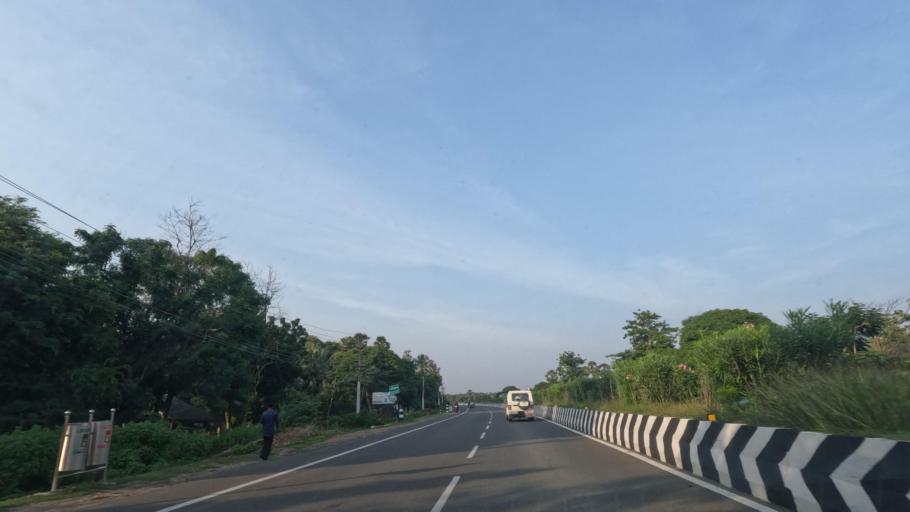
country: IN
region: Tamil Nadu
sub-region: Kancheepuram
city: Mamallapuram
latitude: 12.6571
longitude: 80.2079
